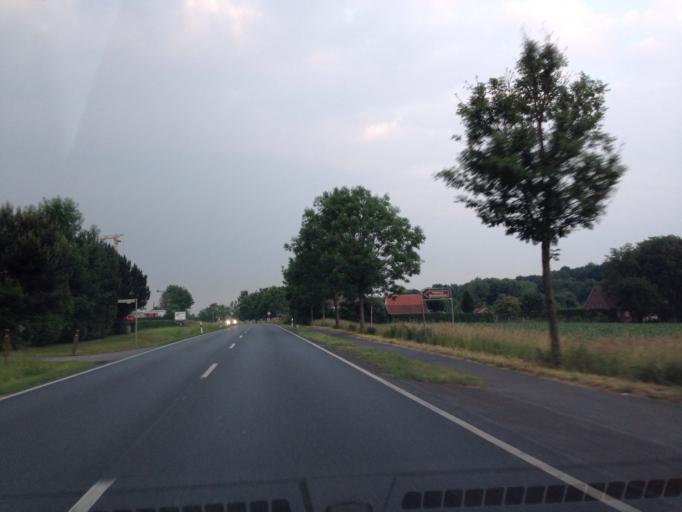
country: DE
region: North Rhine-Westphalia
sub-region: Regierungsbezirk Munster
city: Nottuln
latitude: 51.9240
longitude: 7.3676
